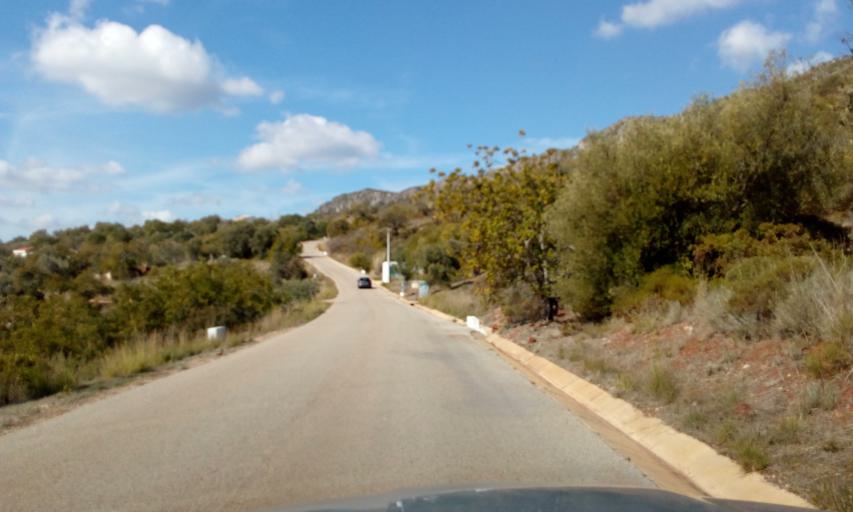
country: PT
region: Faro
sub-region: Loule
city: Boliqueime
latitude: 37.2495
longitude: -8.0924
